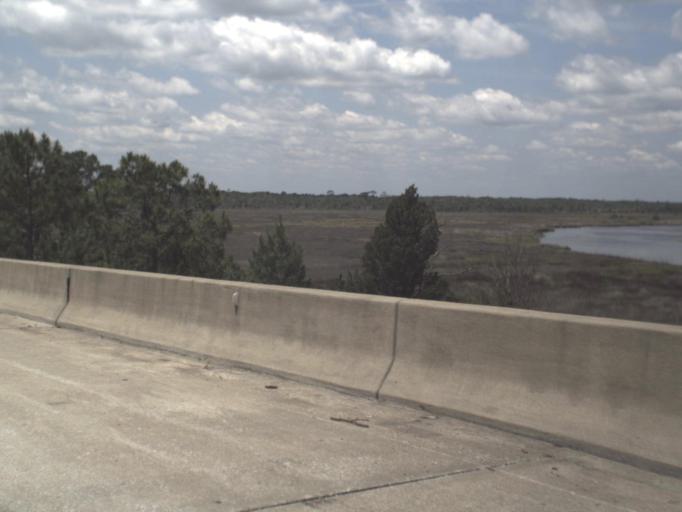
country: US
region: Georgia
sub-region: Camden County
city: Kingsland
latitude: 30.7431
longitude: -81.6550
